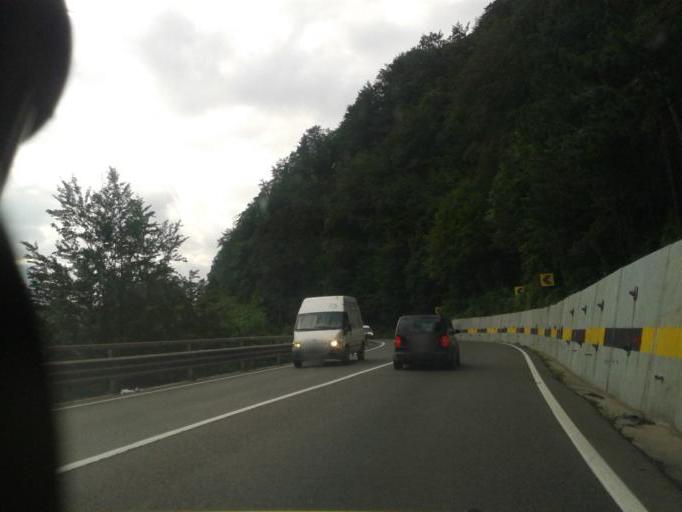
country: RO
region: Prahova
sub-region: Comuna Comarnic
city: Posada
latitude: 45.2937
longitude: 25.6021
